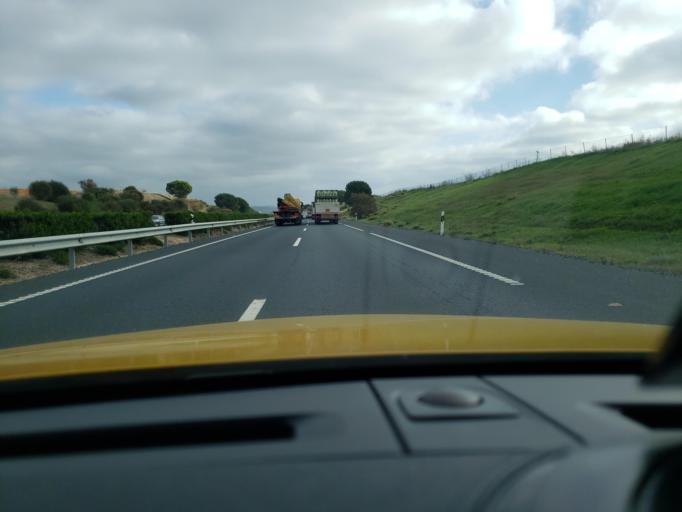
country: ES
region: Andalusia
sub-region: Provincia de Huelva
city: Chucena
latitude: 37.3536
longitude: -6.3683
